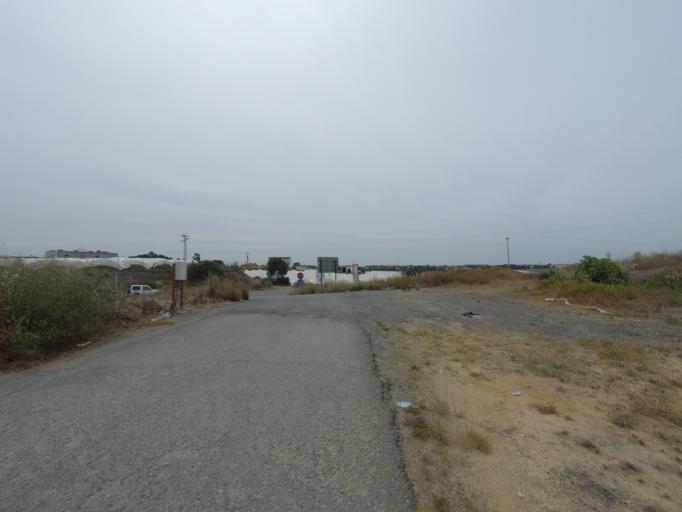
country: ES
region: Andalusia
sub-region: Provincia de Huelva
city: Palos de la Frontera
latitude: 37.2416
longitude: -6.8813
